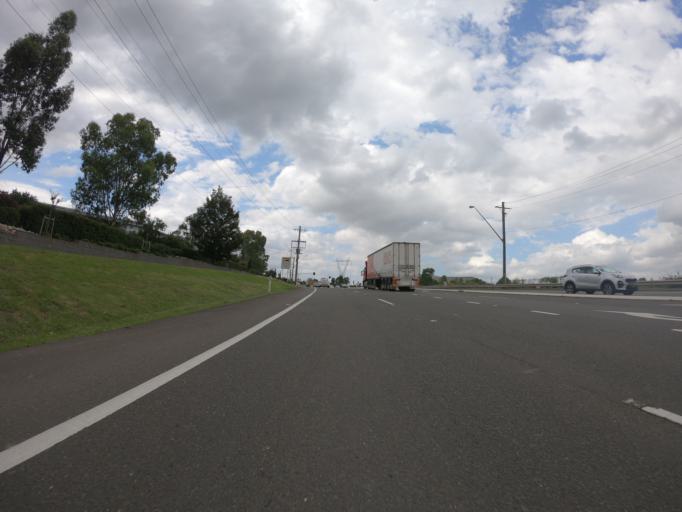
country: AU
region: New South Wales
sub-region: Blacktown
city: Mount Druitt
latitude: -33.8136
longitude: 150.7848
